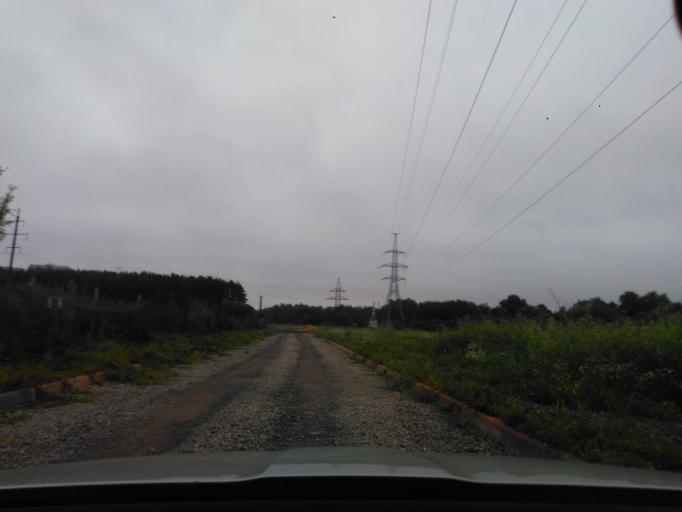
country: RU
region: Moskovskaya
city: Firsanovka
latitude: 55.9391
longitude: 37.2445
